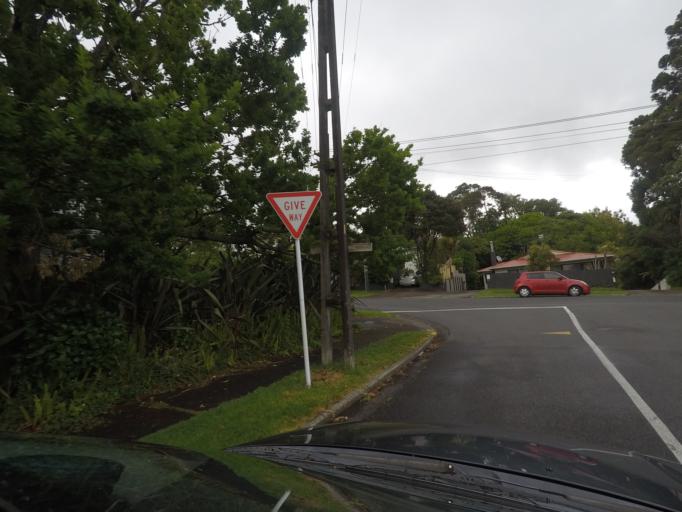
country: NZ
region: Auckland
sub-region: Auckland
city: Auckland
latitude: -36.8936
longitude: 174.7294
